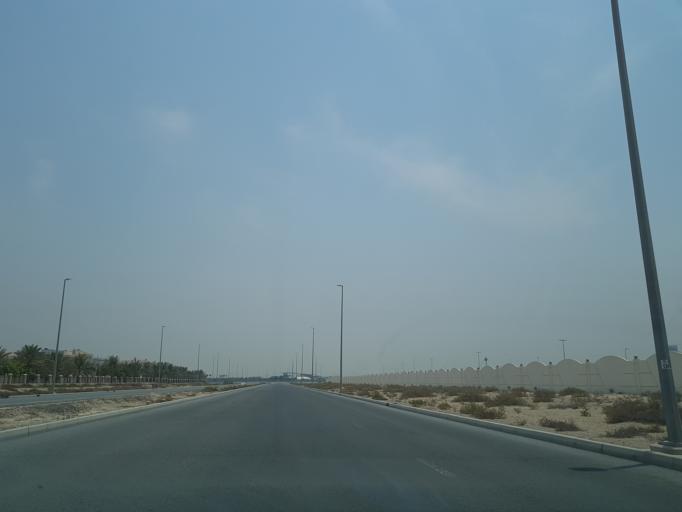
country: AE
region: Dubai
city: Dubai
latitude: 25.0344
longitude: 55.2480
